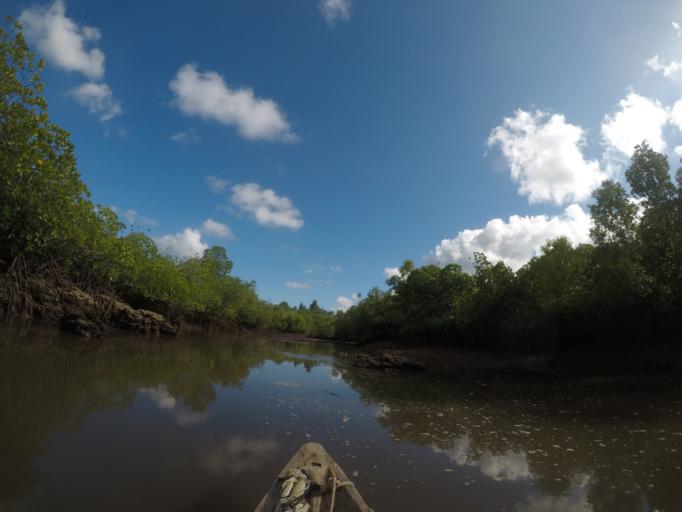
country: TZ
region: Pemba South
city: Mtambile
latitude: -5.3452
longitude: 39.6940
